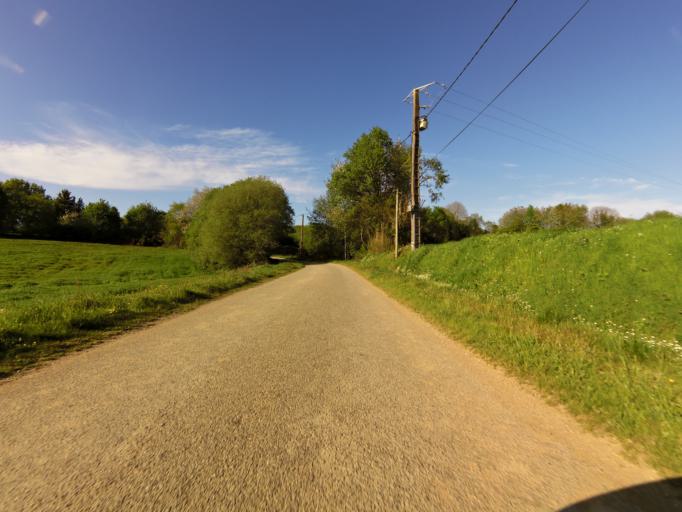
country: FR
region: Brittany
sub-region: Departement du Morbihan
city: Molac
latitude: 47.7330
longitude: -2.4765
